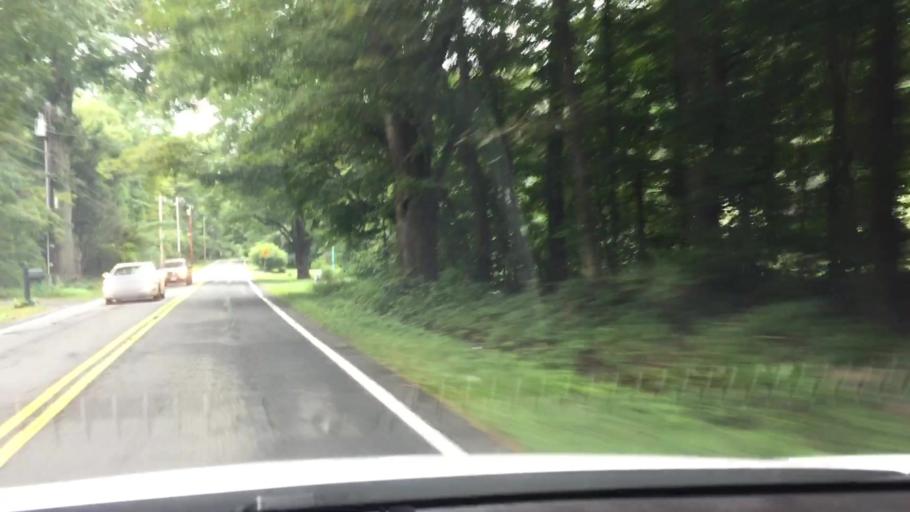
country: US
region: Massachusetts
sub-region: Berkshire County
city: Housatonic
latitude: 42.2373
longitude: -73.3715
